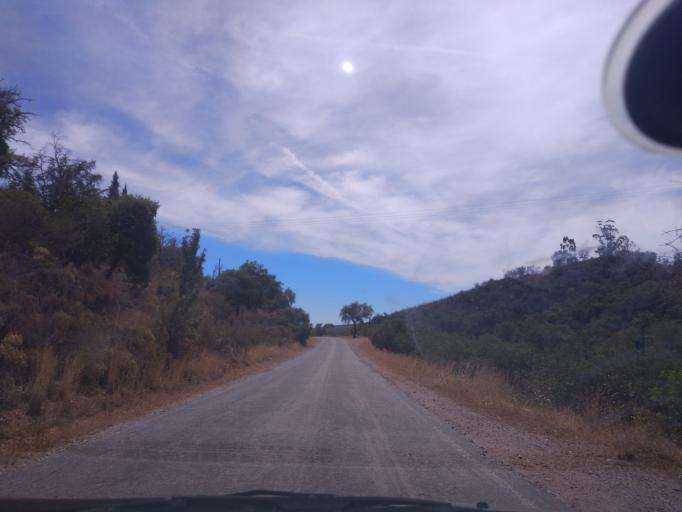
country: PT
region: Faro
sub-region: Olhao
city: Moncarapacho
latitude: 37.1571
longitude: -7.7981
